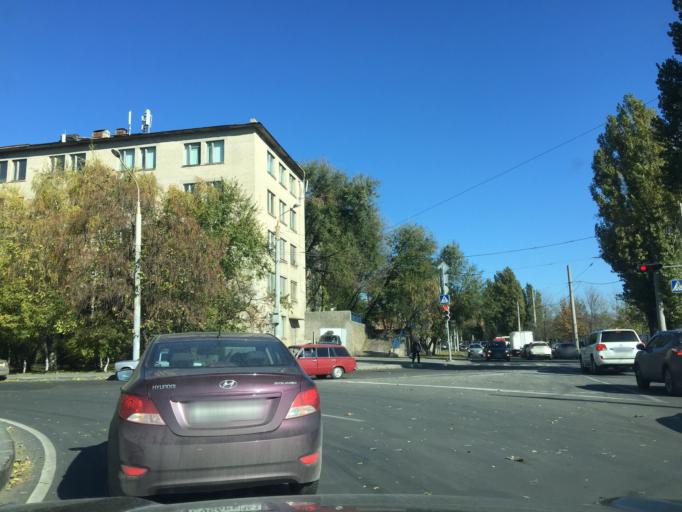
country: RU
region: Rostov
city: Imeni Chkalova
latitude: 47.2486
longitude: 39.7577
